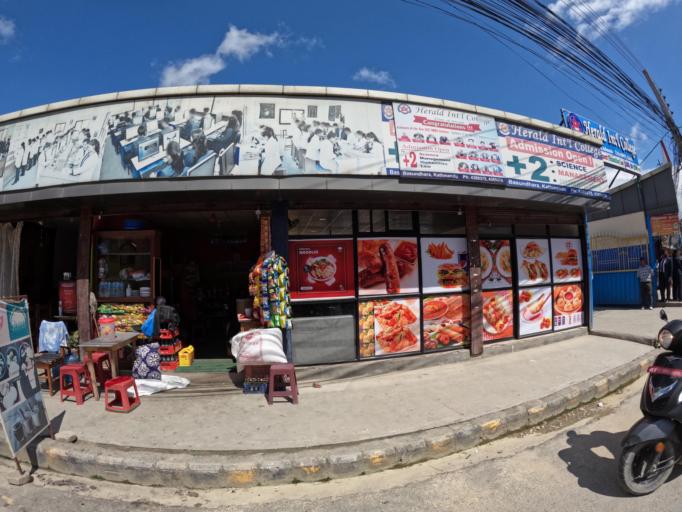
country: NP
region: Central Region
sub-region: Bagmati Zone
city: Kathmandu
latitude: 27.7425
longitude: 85.3294
